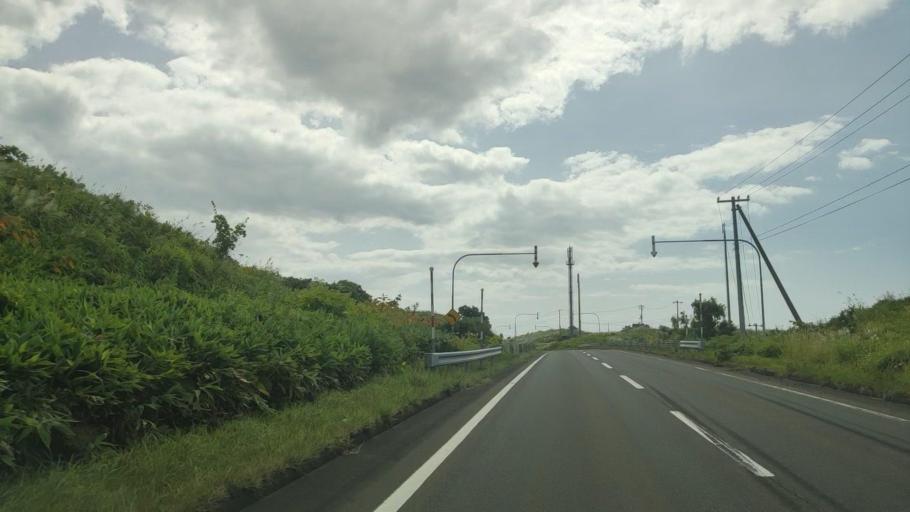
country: JP
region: Hokkaido
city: Rumoi
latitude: 44.6023
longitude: 141.7928
